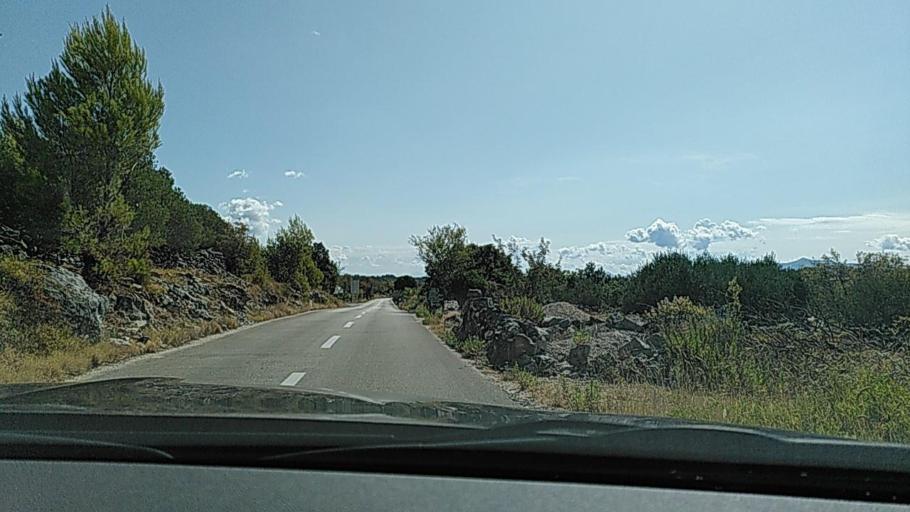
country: HR
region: Splitsko-Dalmatinska
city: Tucepi
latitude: 43.1313
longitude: 16.9804
